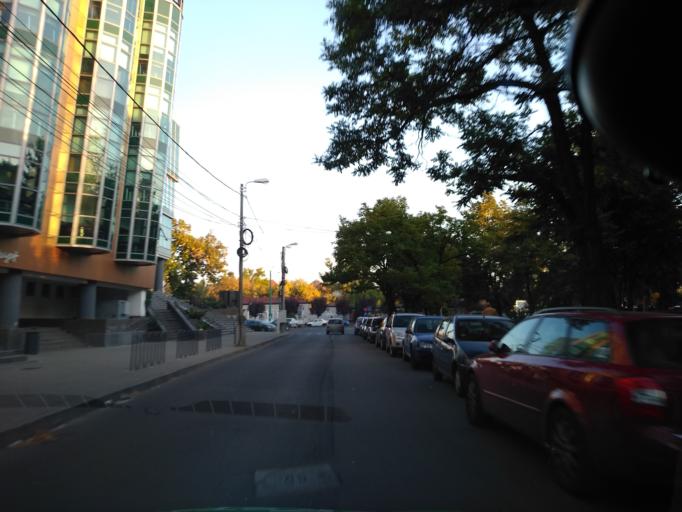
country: RO
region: Timis
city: Timisoara
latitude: 45.7469
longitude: 21.2294
